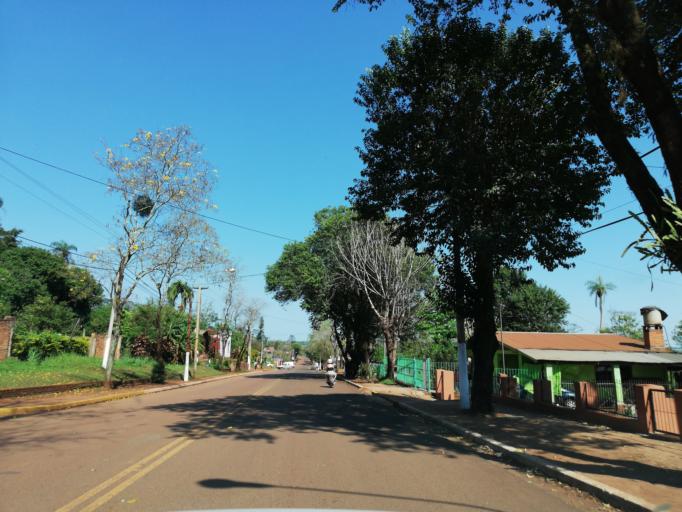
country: AR
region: Misiones
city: Puerto Eldorado
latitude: -26.4093
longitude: -54.6755
